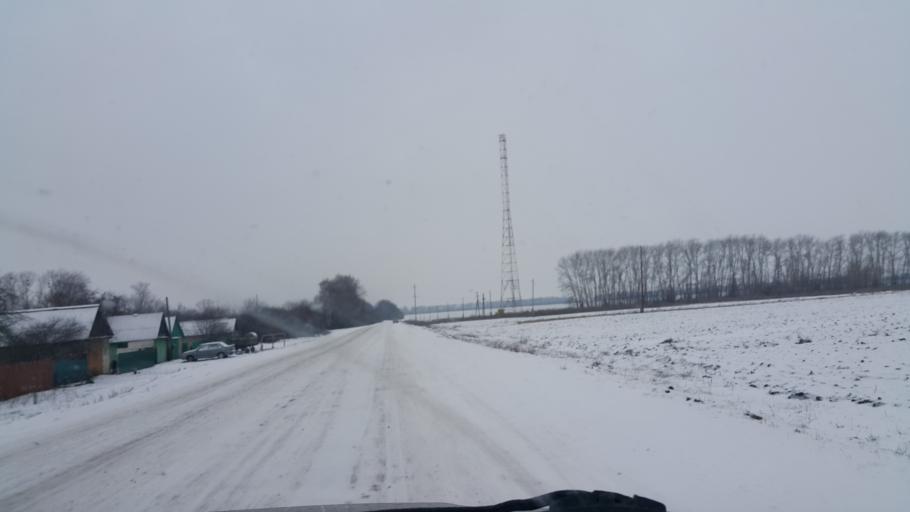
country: RU
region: Tambov
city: Inzhavino
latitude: 52.4692
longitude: 42.3858
